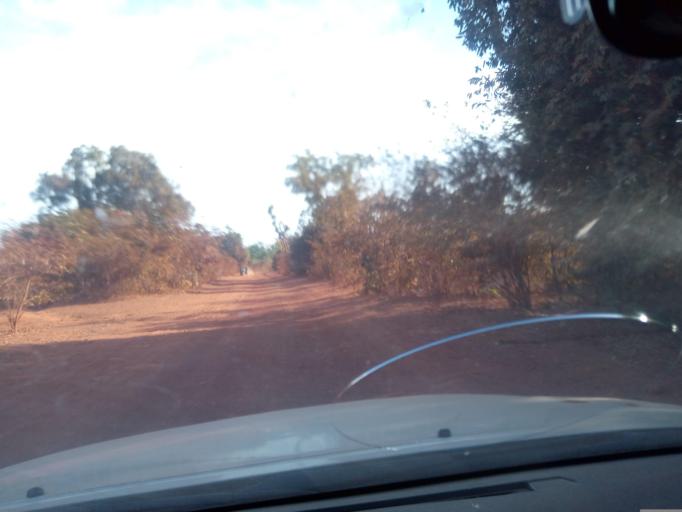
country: ML
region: Sikasso
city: Sikasso
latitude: 11.4347
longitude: -5.5574
